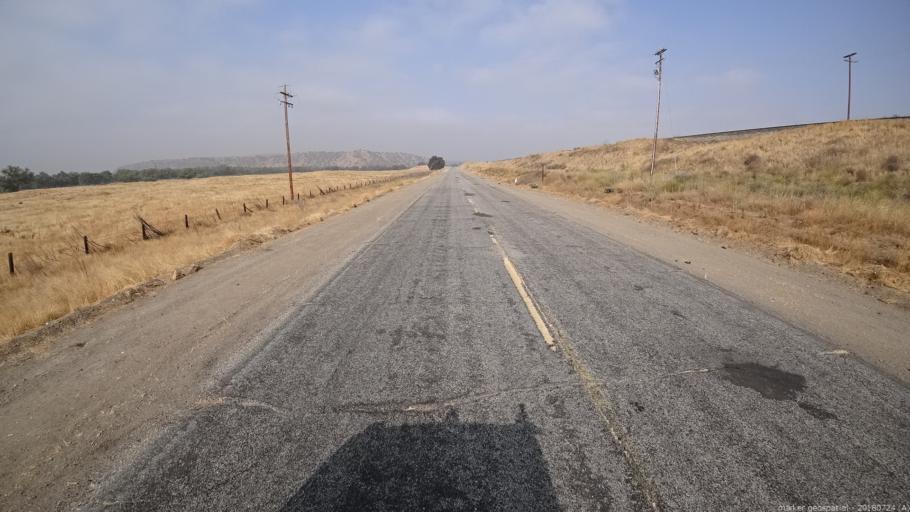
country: US
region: California
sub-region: San Luis Obispo County
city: San Miguel
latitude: 35.8621
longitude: -120.7854
